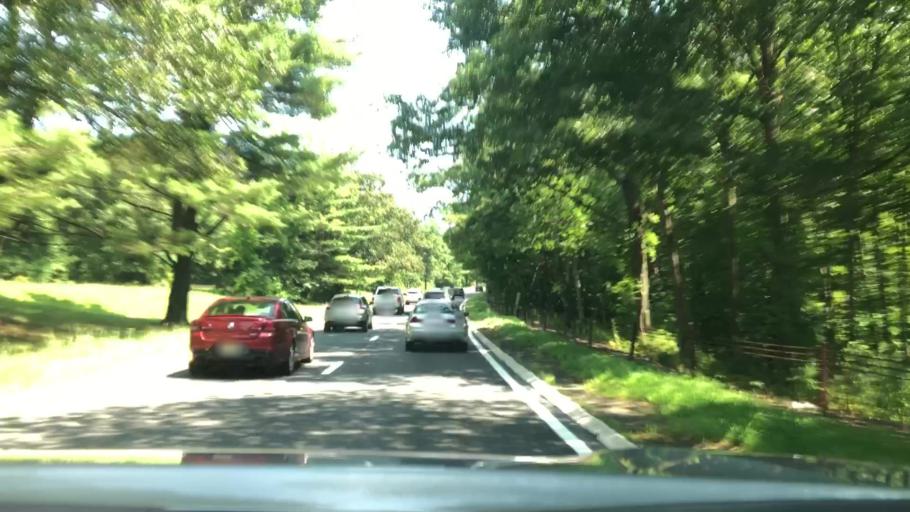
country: US
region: New York
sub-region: Rockland County
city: Thiells
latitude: 41.2624
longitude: -74.0410
